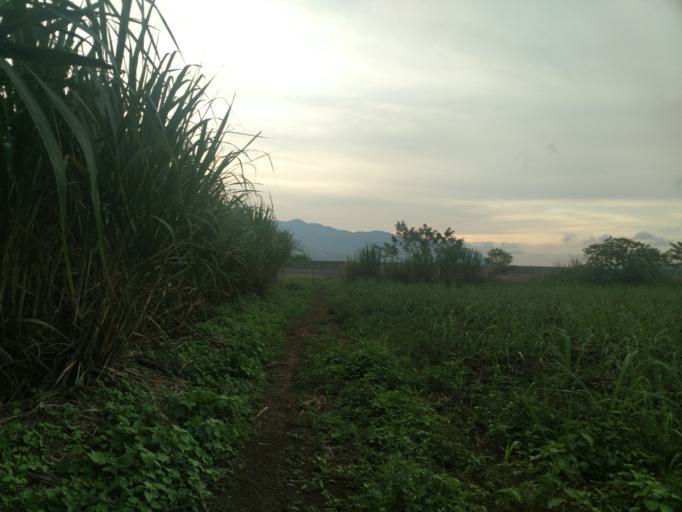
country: MX
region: Nayarit
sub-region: Tepic
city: La Corregidora
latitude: 21.4645
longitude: -104.8104
